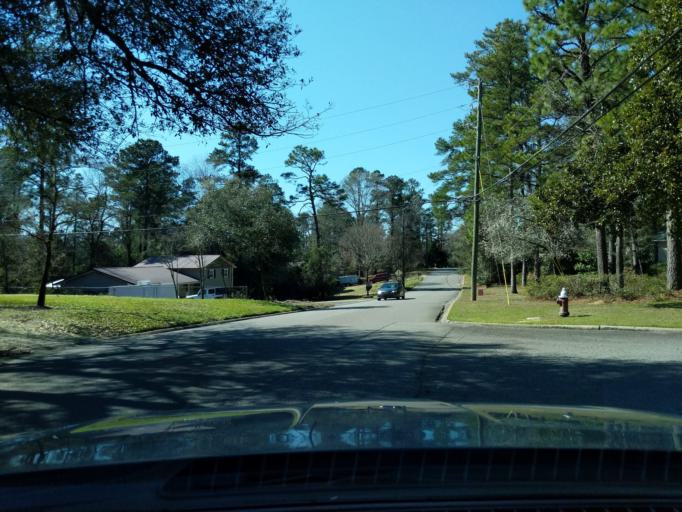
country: US
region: South Carolina
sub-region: Aiken County
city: Aiken
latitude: 33.5280
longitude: -81.7299
